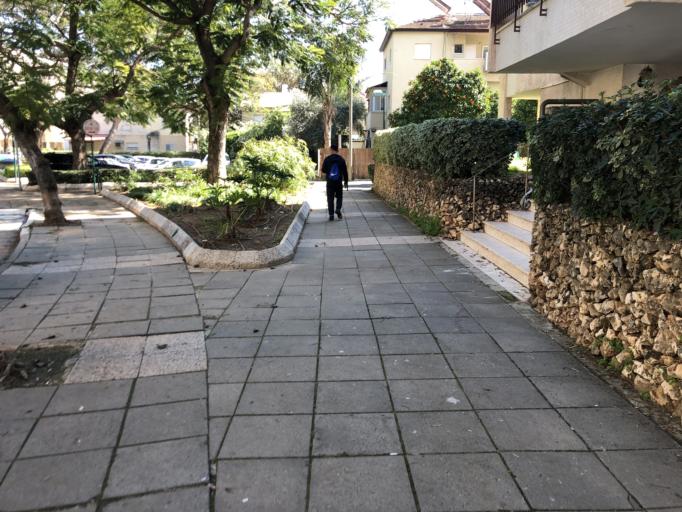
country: IL
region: Central District
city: Kfar Saba
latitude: 32.1753
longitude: 34.9125
